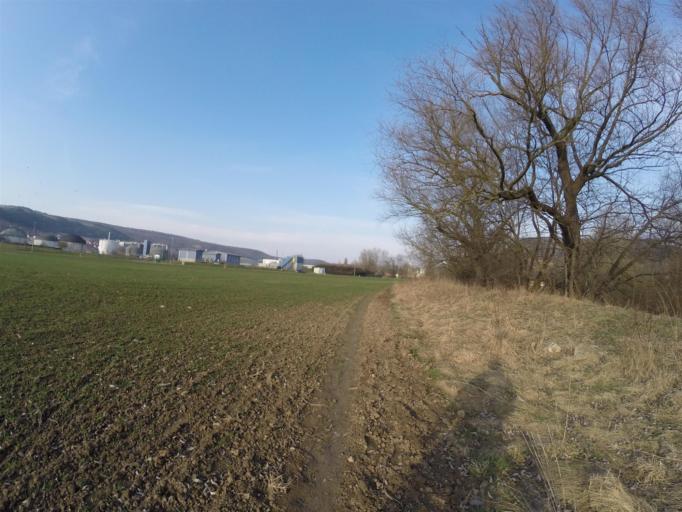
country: DE
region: Thuringia
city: Neuengonna
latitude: 50.9543
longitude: 11.6283
